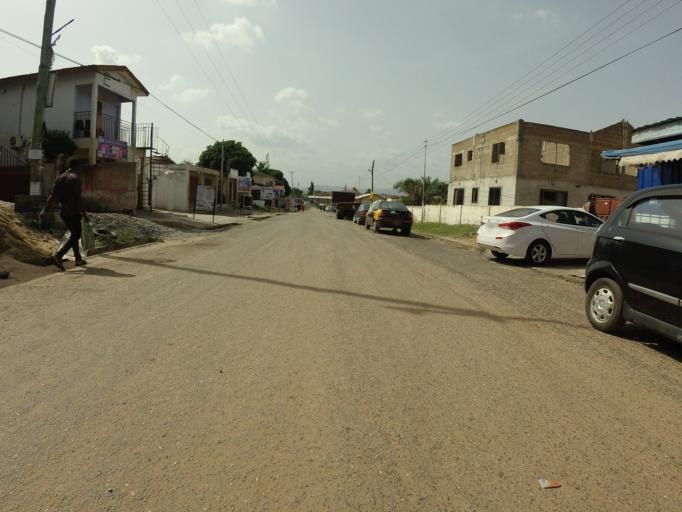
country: GH
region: Greater Accra
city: Dome
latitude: 5.6113
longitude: -0.2395
